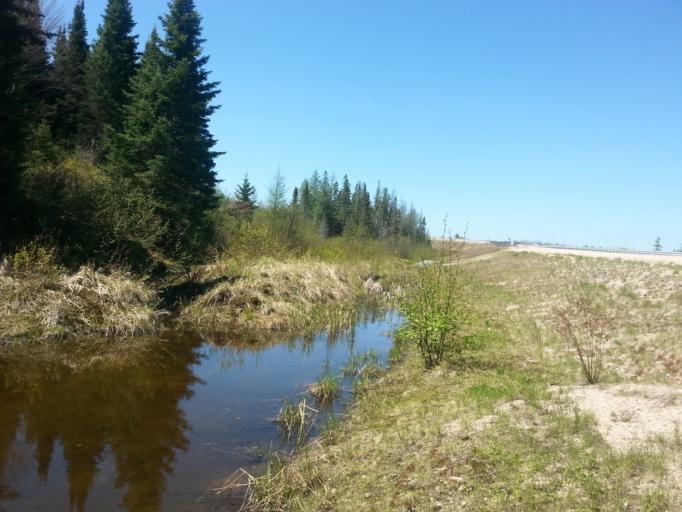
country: CA
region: Ontario
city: South River
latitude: 45.8176
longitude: -79.3939
